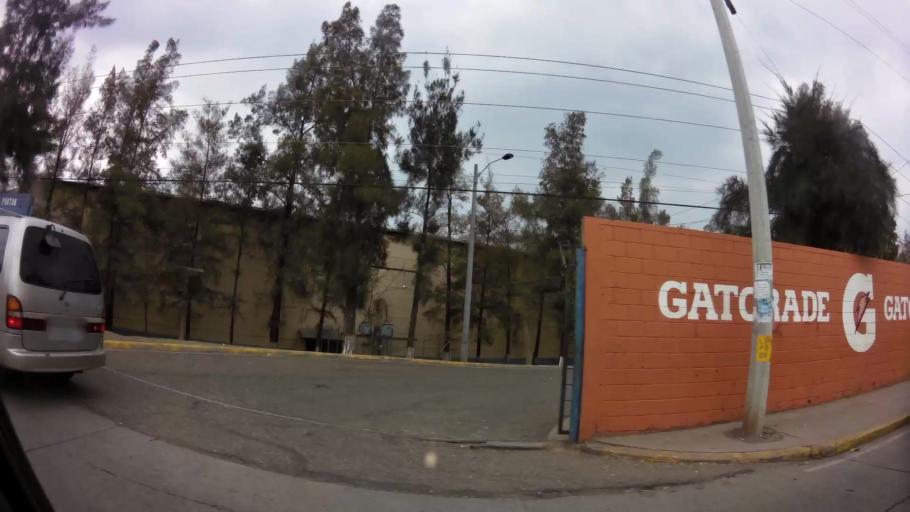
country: HN
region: Francisco Morazan
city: Tegucigalpa
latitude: 14.0917
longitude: -87.1632
